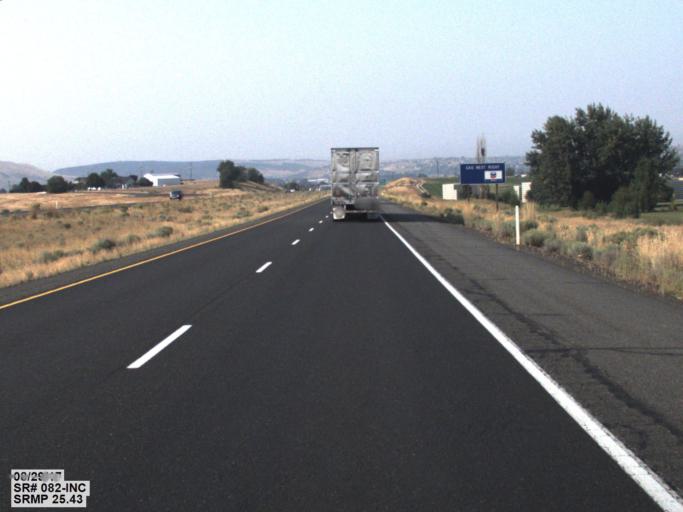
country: US
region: Washington
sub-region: Yakima County
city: Selah
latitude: 46.6879
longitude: -120.4623
